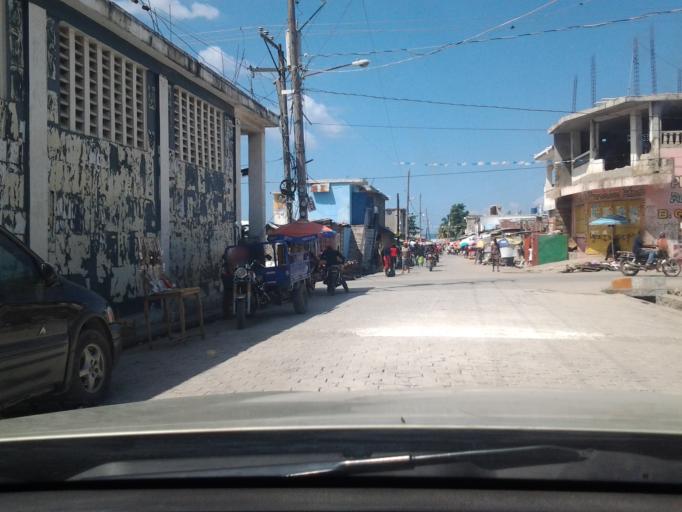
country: HT
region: Ouest
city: Tigwav
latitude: 18.4332
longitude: -72.8651
